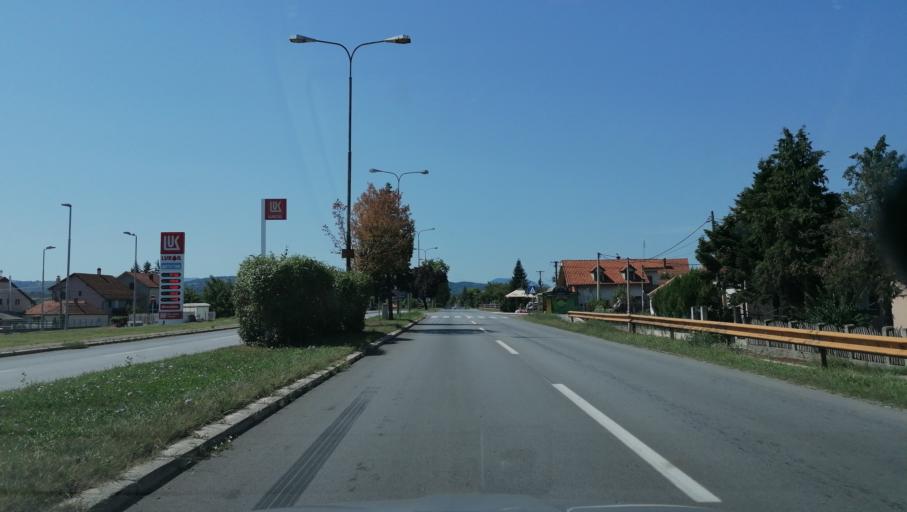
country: RS
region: Central Serbia
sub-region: Kolubarski Okrug
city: Valjevo
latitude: 44.2780
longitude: 19.9178
